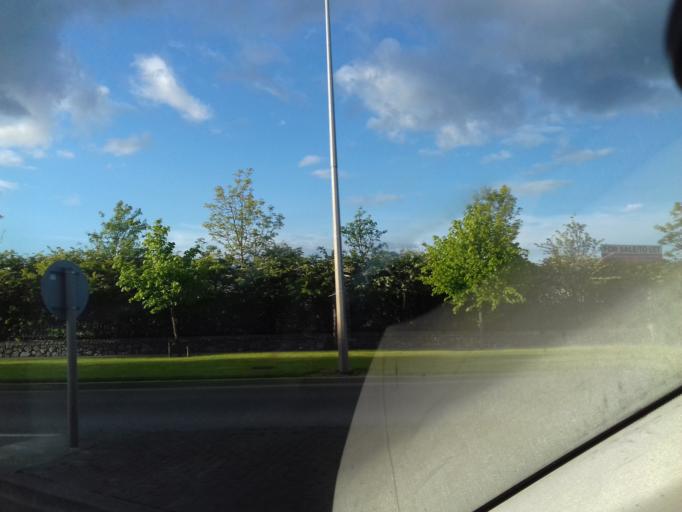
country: IE
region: Leinster
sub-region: South Dublin
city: Rathcoole
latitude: 53.2901
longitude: -6.4676
